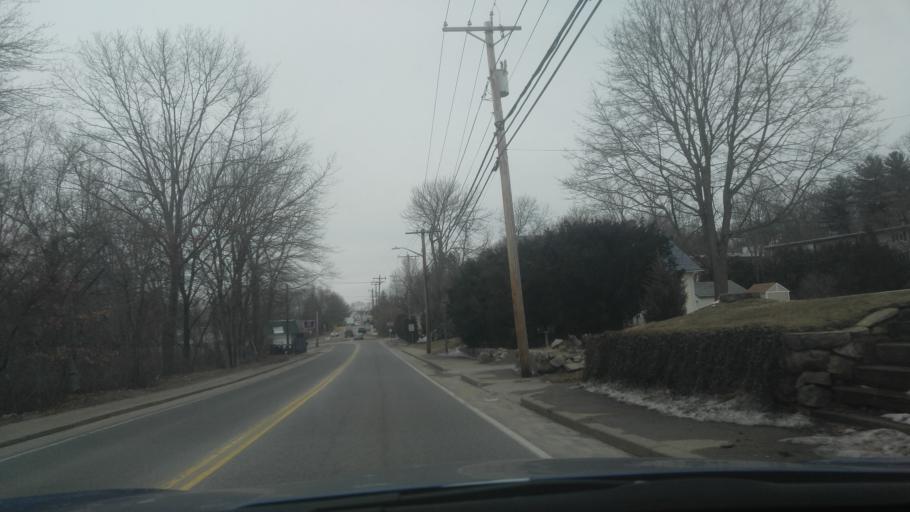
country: US
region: Rhode Island
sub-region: Kent County
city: West Warwick
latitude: 41.6797
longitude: -71.5269
